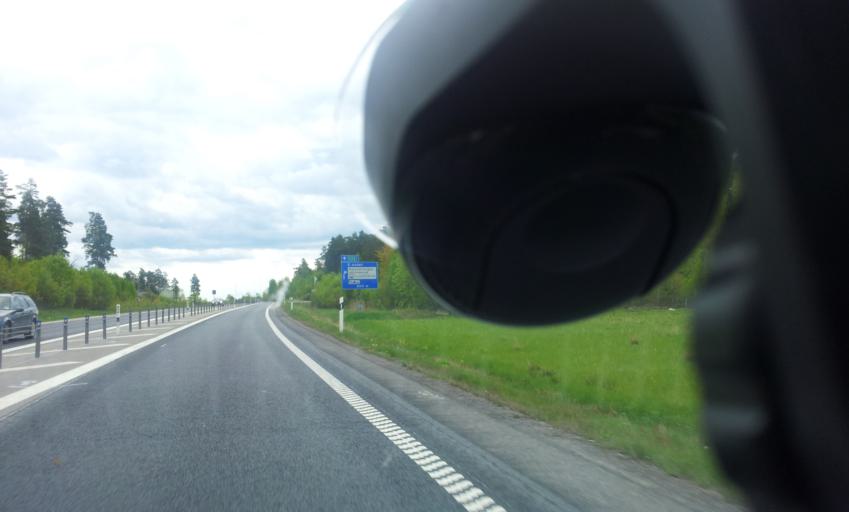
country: SE
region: OEstergoetland
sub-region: Soderkopings Kommun
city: Soederkoeping
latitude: 58.5004
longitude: 16.3014
